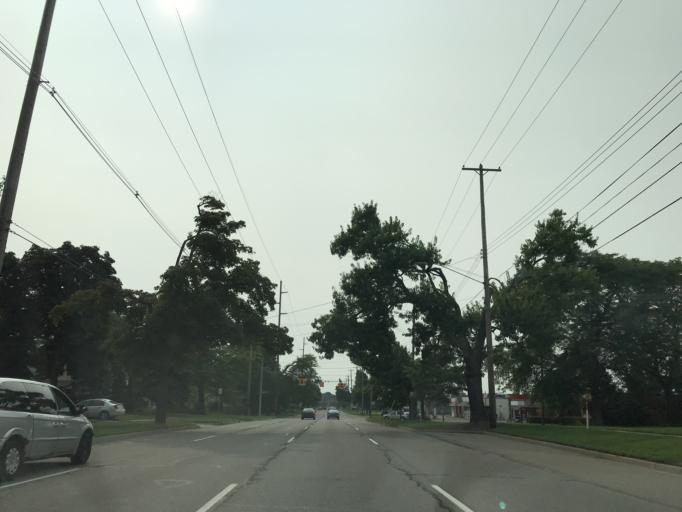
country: US
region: Michigan
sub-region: Ingham County
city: East Lansing
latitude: 42.7433
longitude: -84.5161
